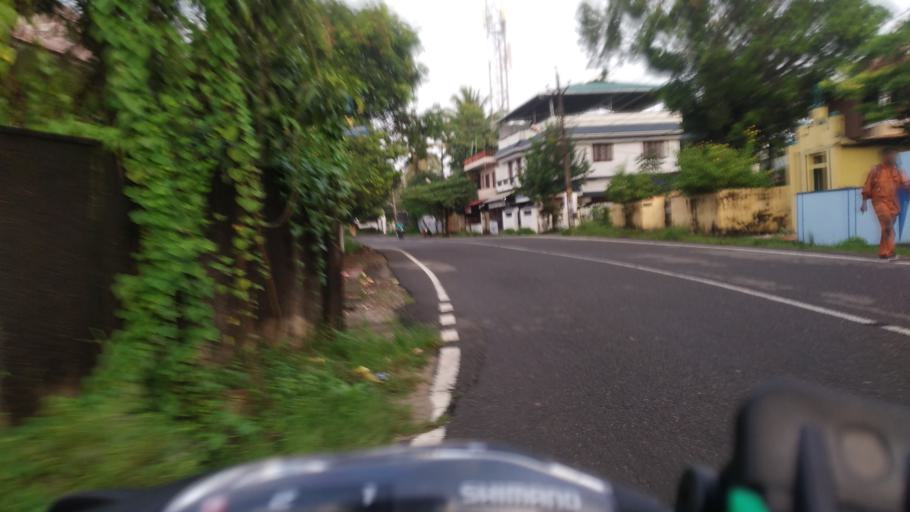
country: IN
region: Kerala
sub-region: Ernakulam
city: Cochin
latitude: 9.9743
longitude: 76.2435
